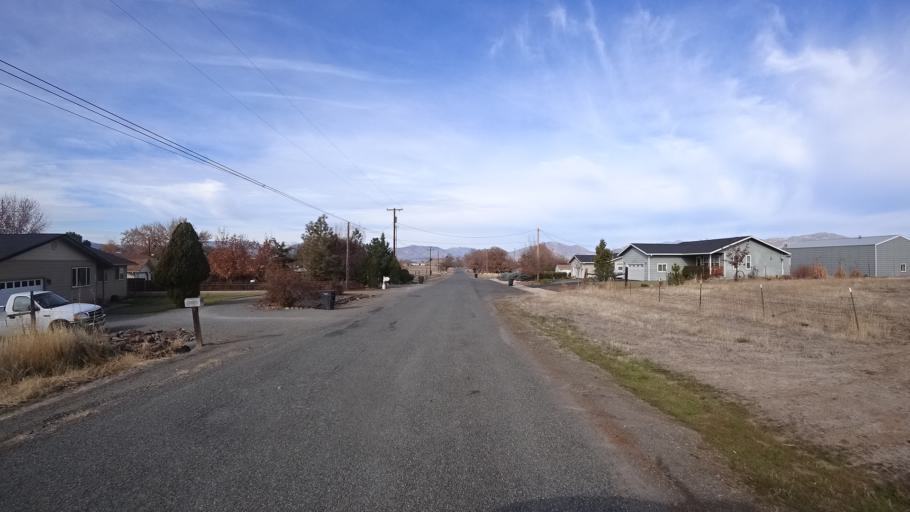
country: US
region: California
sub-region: Siskiyou County
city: Montague
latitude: 41.7204
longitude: -122.5229
